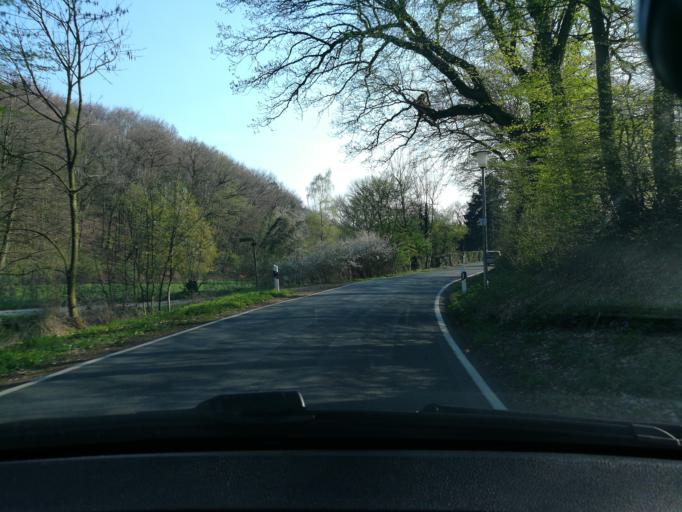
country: DE
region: North Rhine-Westphalia
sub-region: Regierungsbezirk Detmold
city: Steinhagen
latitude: 52.0279
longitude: 8.4220
